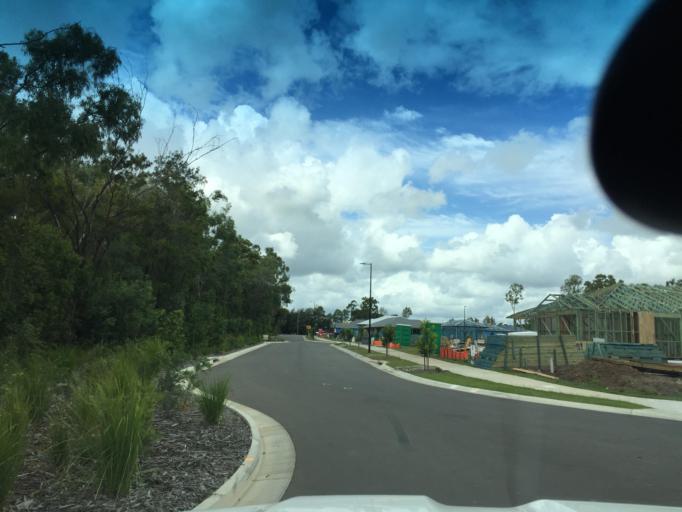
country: AU
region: Queensland
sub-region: Moreton Bay
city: Burpengary
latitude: -27.1628
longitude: 152.9841
